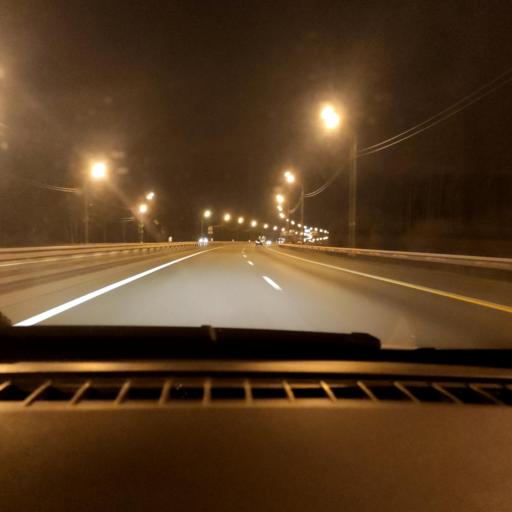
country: RU
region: Lipetsk
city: Khlevnoye
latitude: 52.2544
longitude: 39.0666
